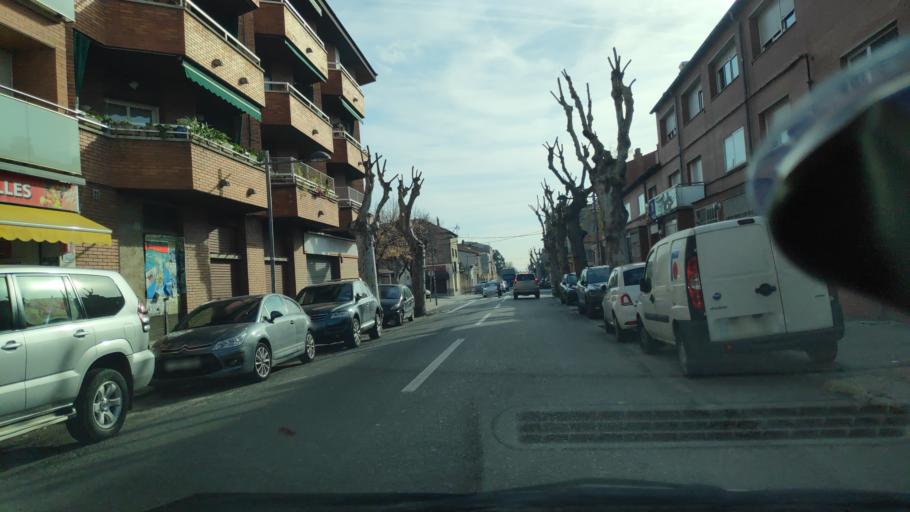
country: ES
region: Catalonia
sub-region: Provincia de Barcelona
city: Castellar del Valles
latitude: 41.6133
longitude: 2.0830
